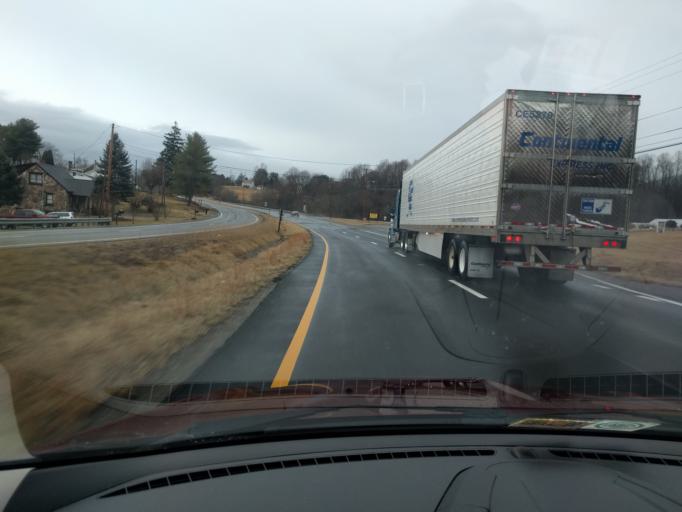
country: US
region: Virginia
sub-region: Giles County
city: Pembroke
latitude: 37.3204
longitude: -80.5916
